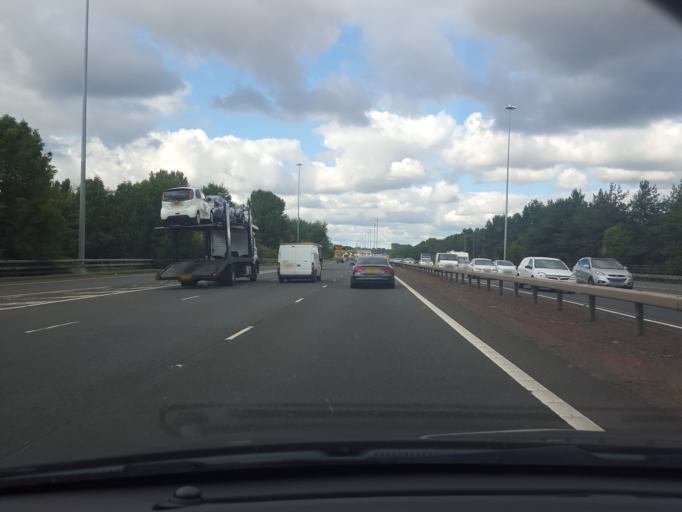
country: GB
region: Scotland
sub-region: South Lanarkshire
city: Hamilton
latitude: 55.7836
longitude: -4.0260
